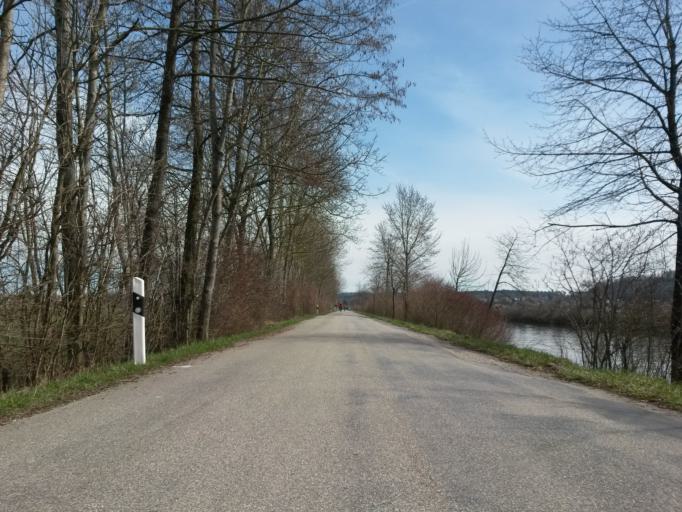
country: CH
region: Bern
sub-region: Biel/Bienne District
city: Meinisberg
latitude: 47.1428
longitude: 7.3539
